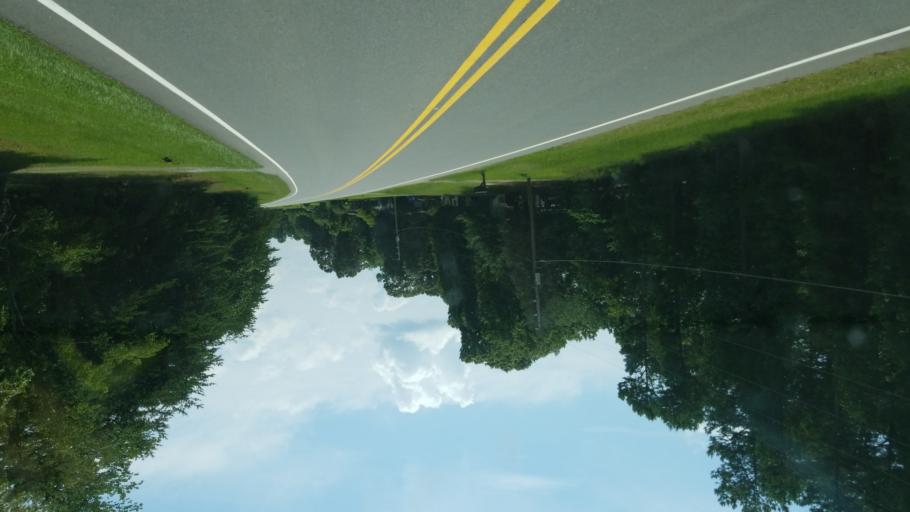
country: US
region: North Carolina
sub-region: Cleveland County
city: Kings Mountain
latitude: 35.1764
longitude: -81.3264
